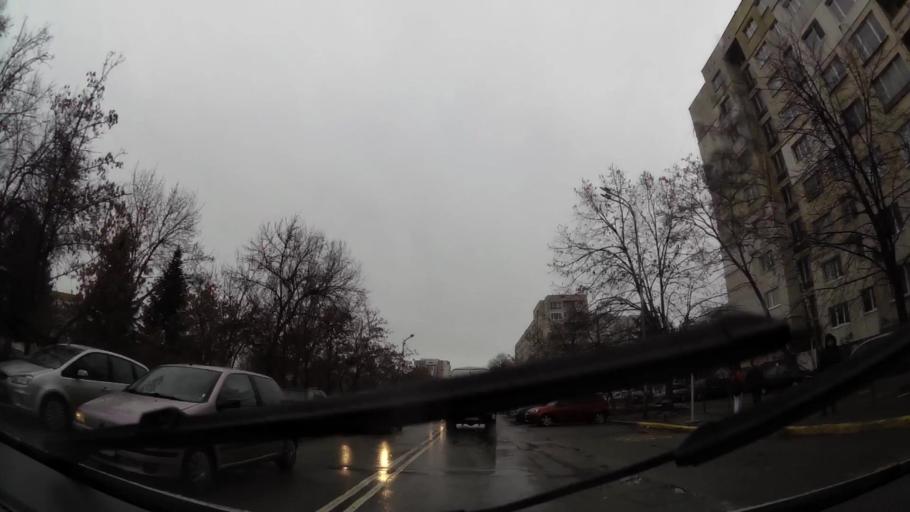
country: BG
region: Sofia-Capital
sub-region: Stolichna Obshtina
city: Sofia
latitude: 42.6403
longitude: 23.3772
